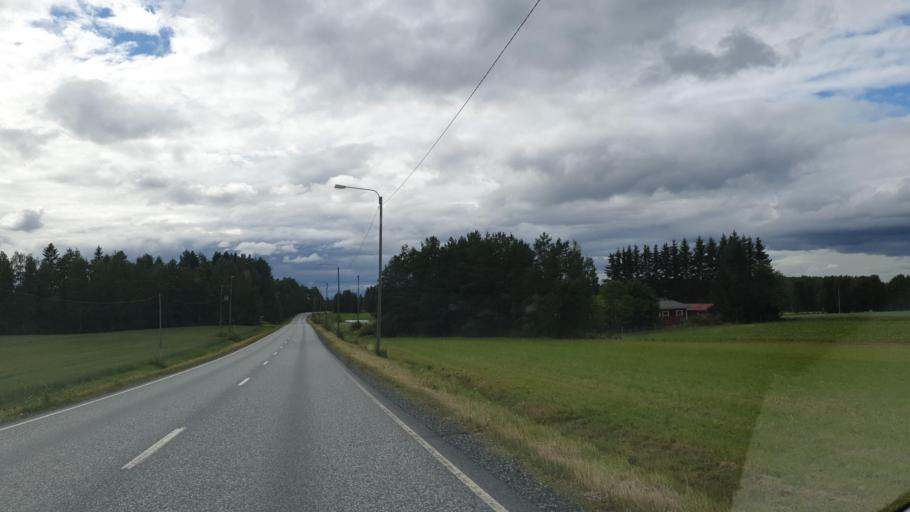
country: FI
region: Northern Savo
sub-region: Ylae-Savo
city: Iisalmi
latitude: 63.5210
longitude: 27.1627
